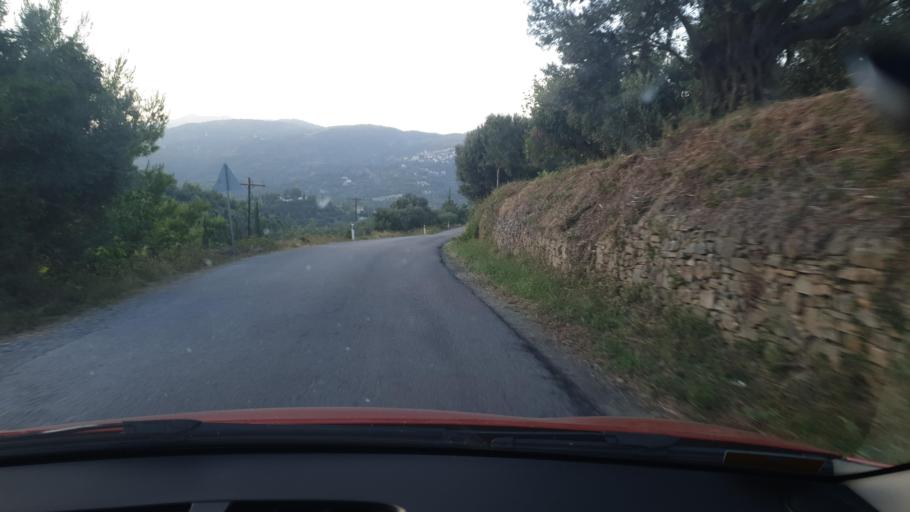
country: GR
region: Central Greece
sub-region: Nomos Evvoias
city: Oxilithos
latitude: 38.5958
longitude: 24.1171
